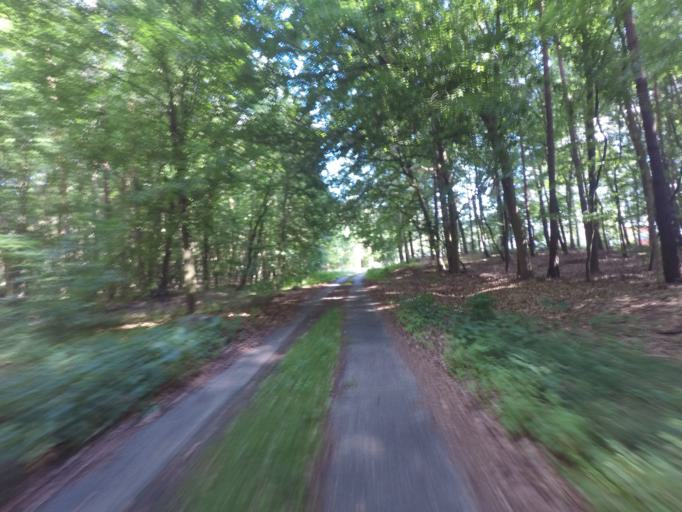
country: DE
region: Brandenburg
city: Britz
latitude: 52.8607
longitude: 13.7874
